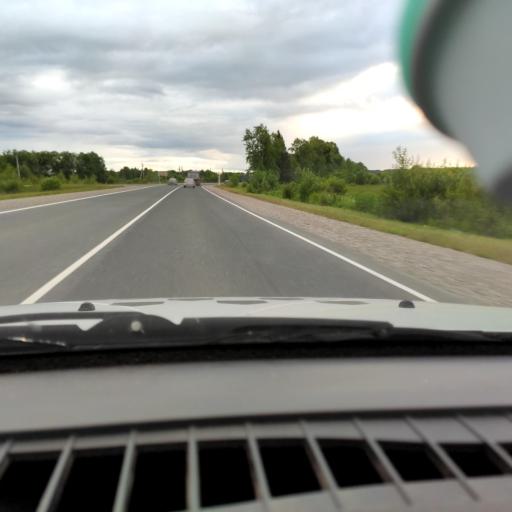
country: RU
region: Perm
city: Kalino
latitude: 58.2893
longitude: 57.4617
